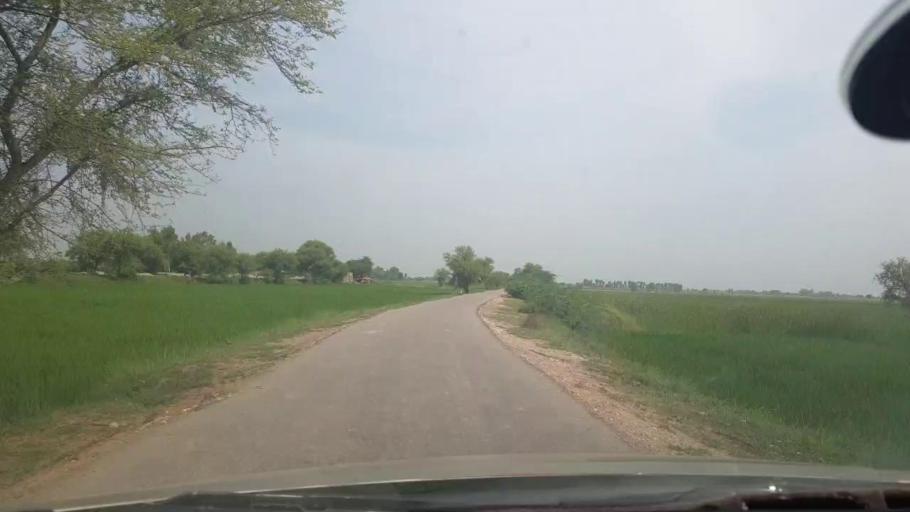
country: PK
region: Sindh
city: Jacobabad
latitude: 28.3021
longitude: 68.4750
